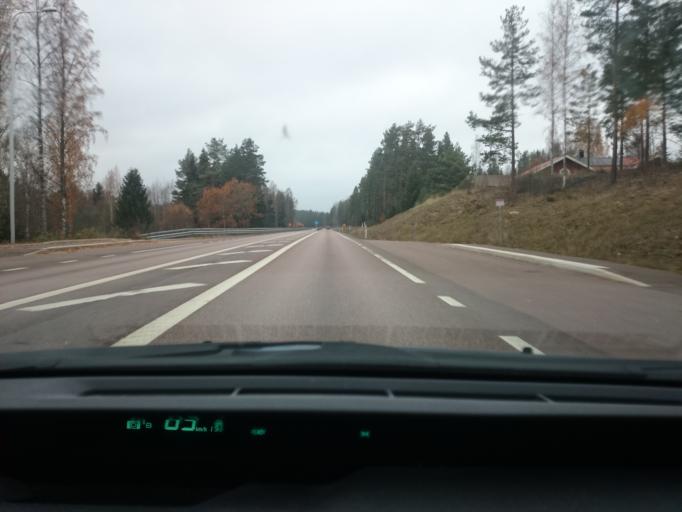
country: SE
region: Dalarna
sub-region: Avesta Kommun
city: Avesta
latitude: 60.1886
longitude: 16.1188
